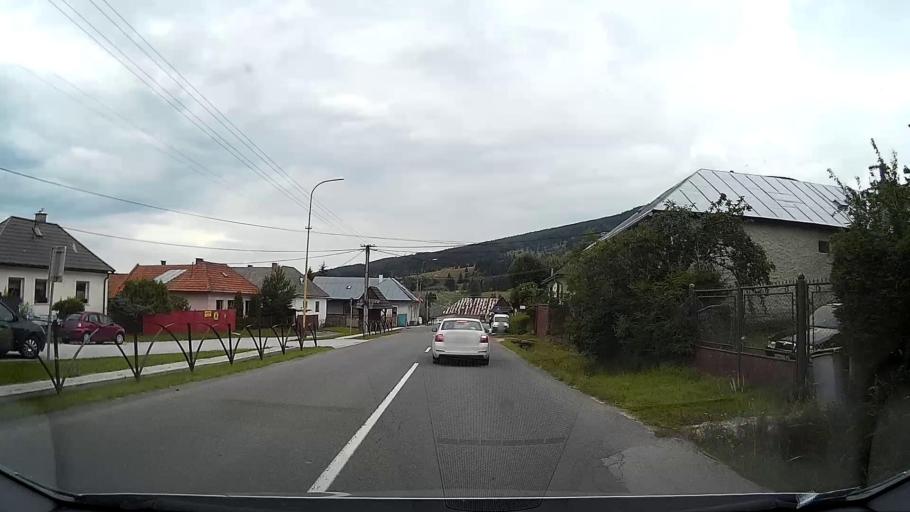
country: SK
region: Kosicky
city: Dobsina
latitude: 48.8515
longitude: 20.1903
